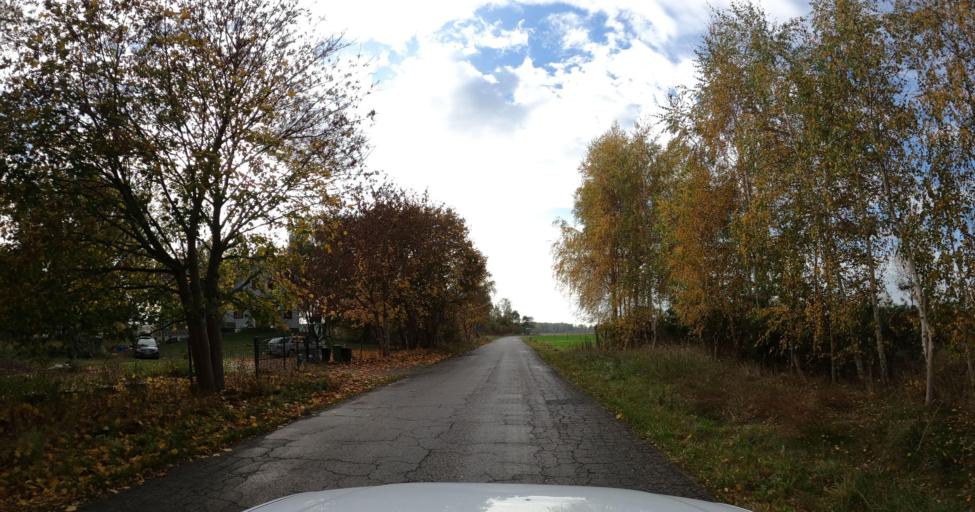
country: PL
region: West Pomeranian Voivodeship
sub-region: Powiat kamienski
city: Kamien Pomorski
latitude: 53.9679
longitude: 14.8450
